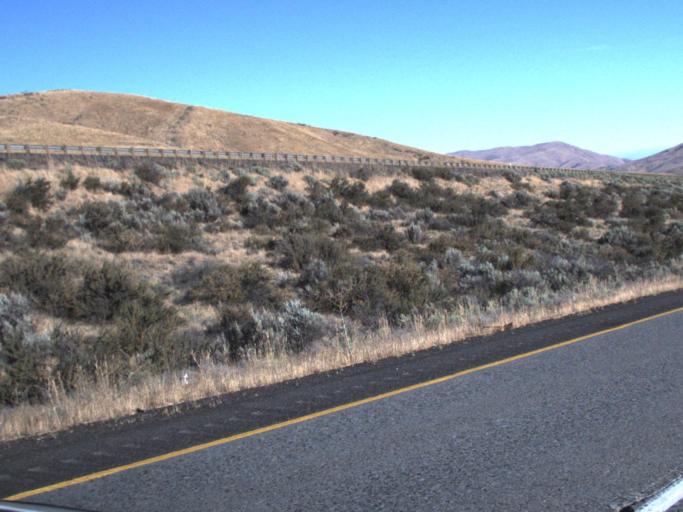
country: US
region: Washington
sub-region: Yakima County
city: Terrace Heights
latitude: 46.7377
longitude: -120.3857
